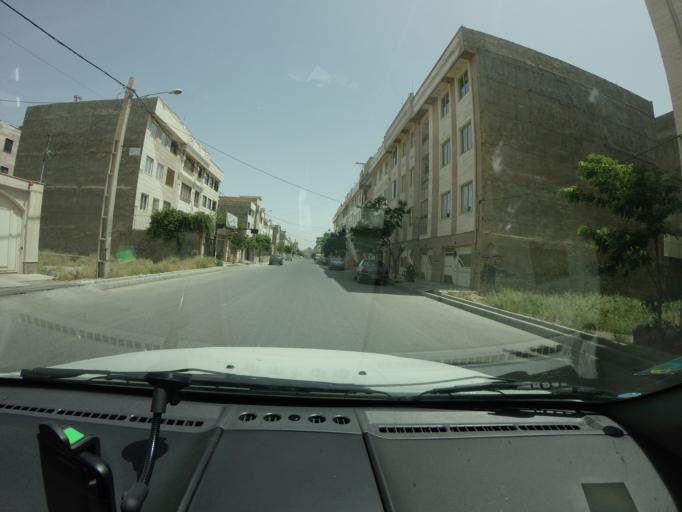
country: IR
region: Tehran
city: Eslamshahr
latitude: 35.5320
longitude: 51.2122
